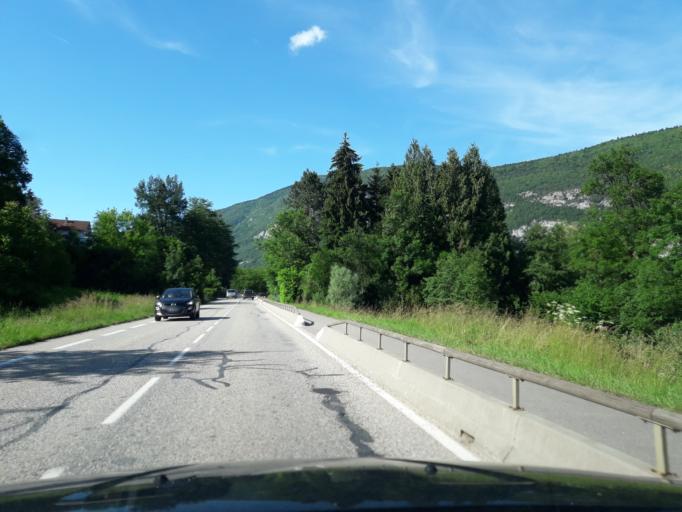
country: FR
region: Rhone-Alpes
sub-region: Departement de la Savoie
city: Novalaise
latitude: 45.5684
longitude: 5.7942
